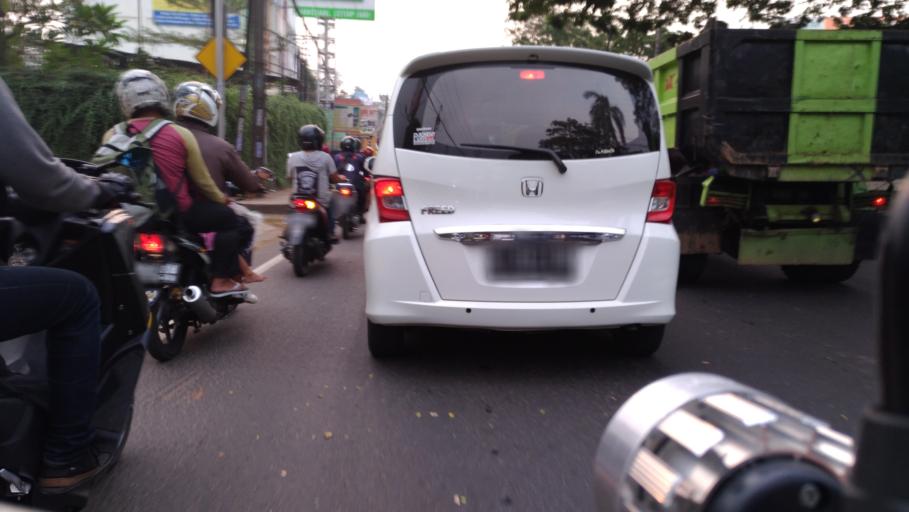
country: ID
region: West Java
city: Cileungsir
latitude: -6.3847
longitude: 106.9353
